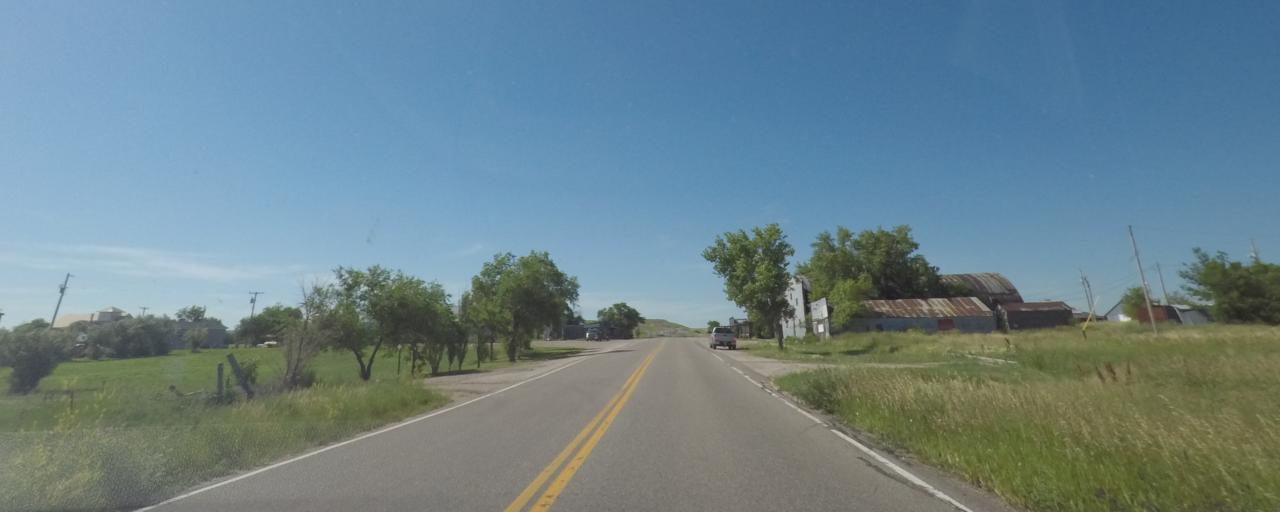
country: US
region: South Dakota
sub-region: Shannon County
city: Porcupine
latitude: 43.7810
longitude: -102.5549
